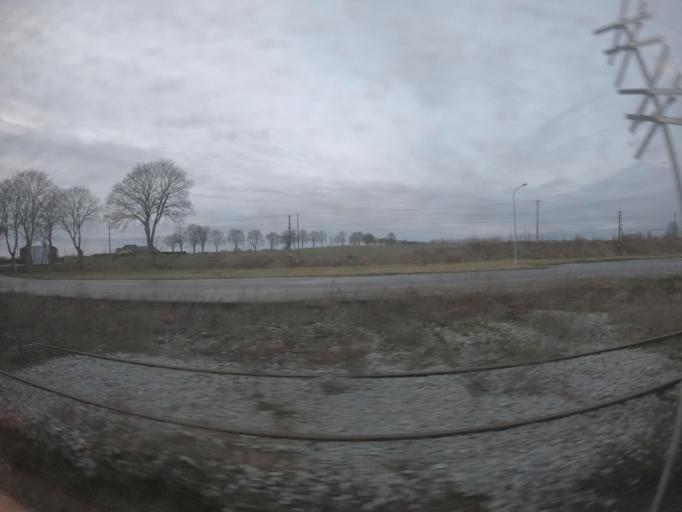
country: PL
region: West Pomeranian Voivodeship
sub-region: Powiat drawski
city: Czaplinek
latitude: 53.5367
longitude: 16.2347
